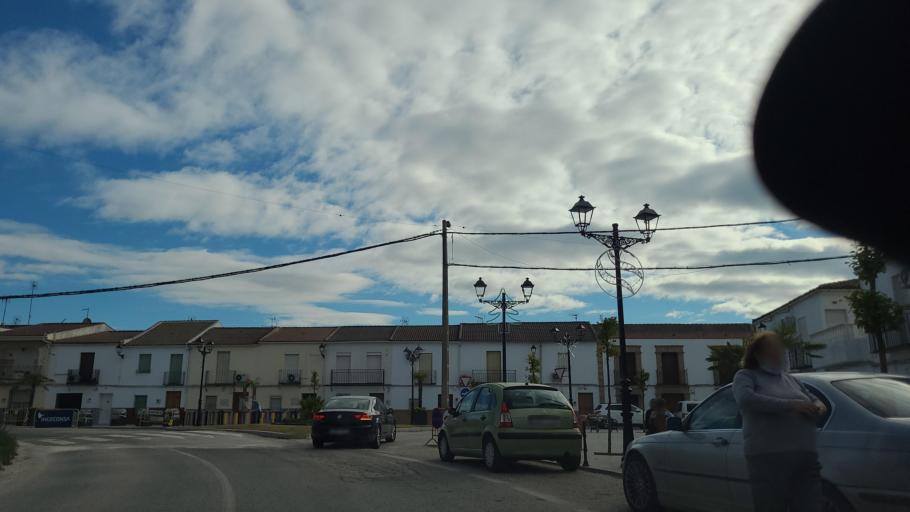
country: ES
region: Andalusia
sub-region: Provincia de Jaen
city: Villanueva de la Reina
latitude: 38.0064
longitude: -3.9128
